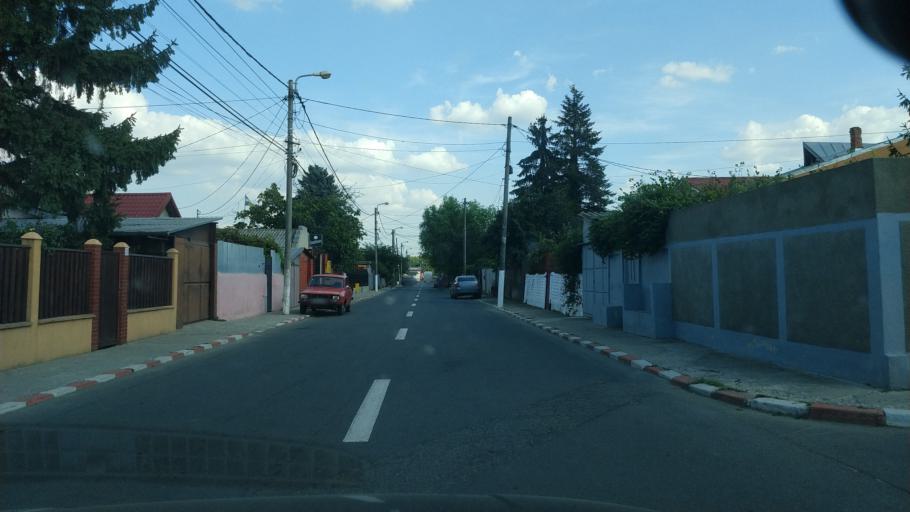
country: RO
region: Ilfov
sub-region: Voluntari City
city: Voluntari
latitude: 44.4906
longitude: 26.1672
